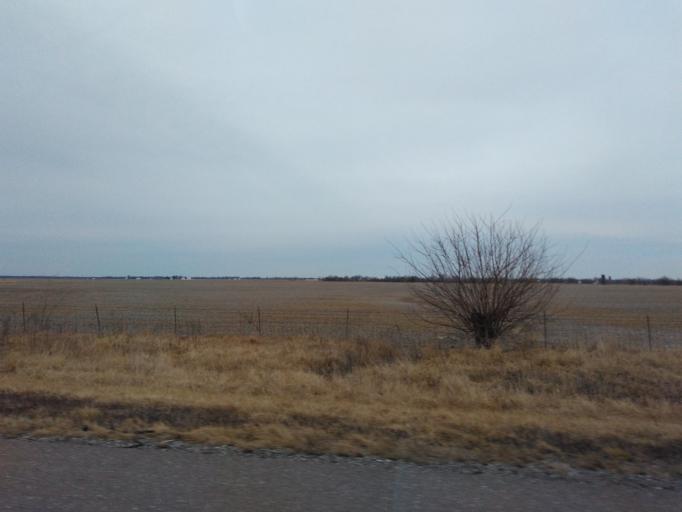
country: US
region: Illinois
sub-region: Washington County
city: Okawville
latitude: 38.4227
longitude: -89.4543
